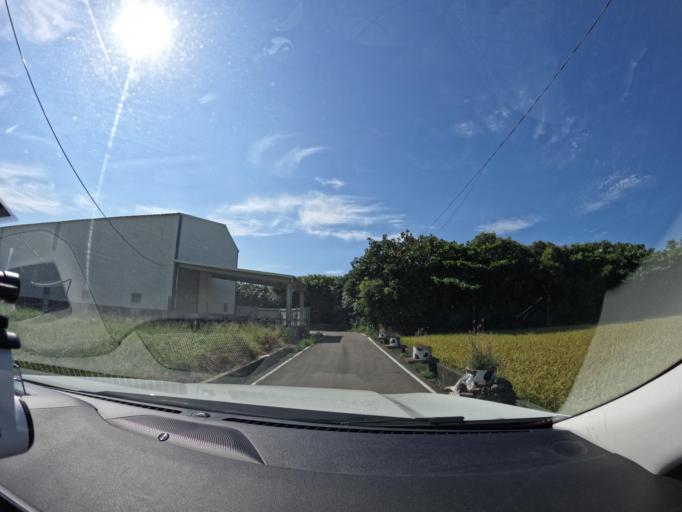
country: TW
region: Taiwan
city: Taoyuan City
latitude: 25.0925
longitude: 121.1900
